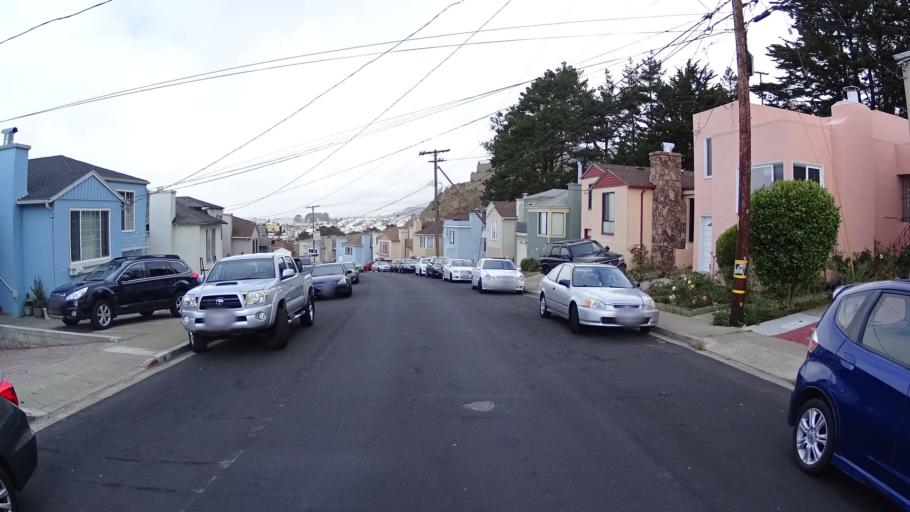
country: US
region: California
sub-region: San Mateo County
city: Daly City
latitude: 37.7020
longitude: -122.4601
